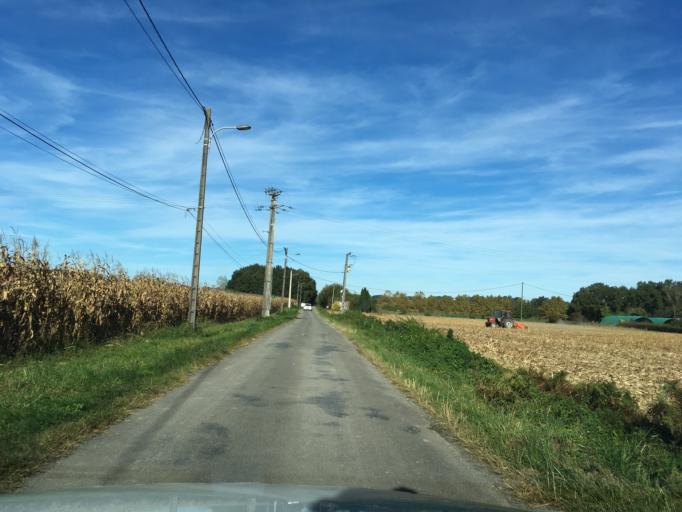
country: FR
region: Aquitaine
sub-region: Departement des Pyrenees-Atlantiques
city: Montardon
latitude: 43.3329
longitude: -0.3409
